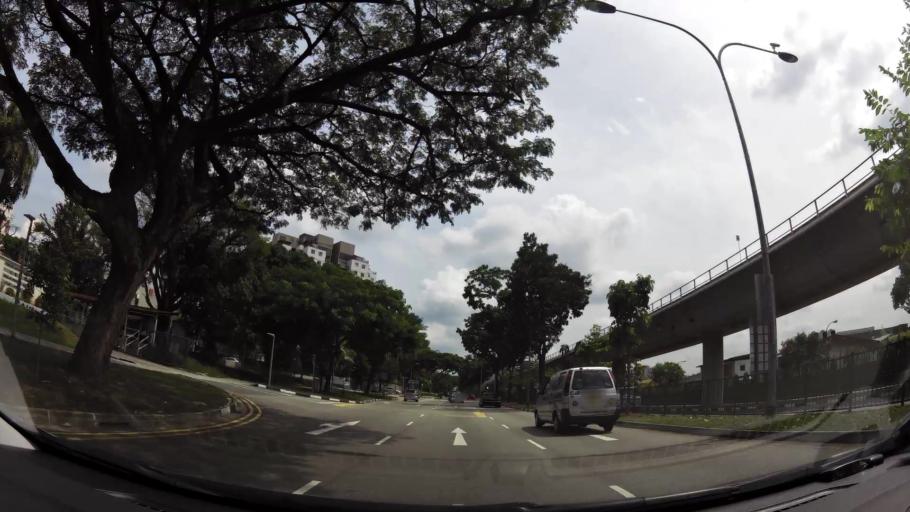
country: MY
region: Johor
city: Johor Bahru
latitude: 1.3410
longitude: 103.7107
